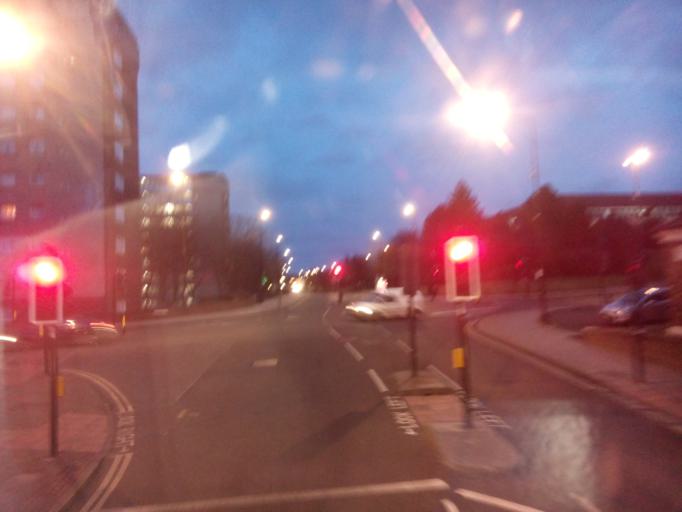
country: GB
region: England
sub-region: Gateshead
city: Gateshead
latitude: 54.9612
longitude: -1.6029
